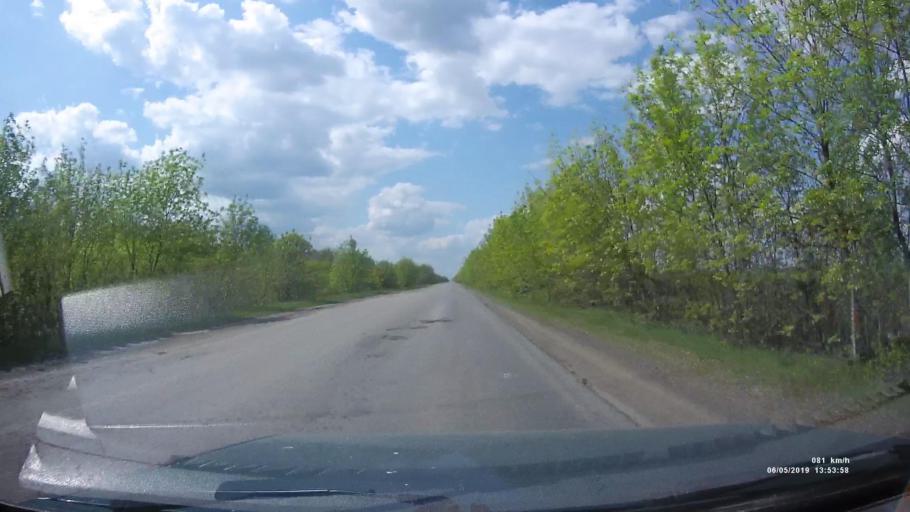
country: RU
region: Rostov
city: Melikhovskaya
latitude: 47.6716
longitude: 40.4543
